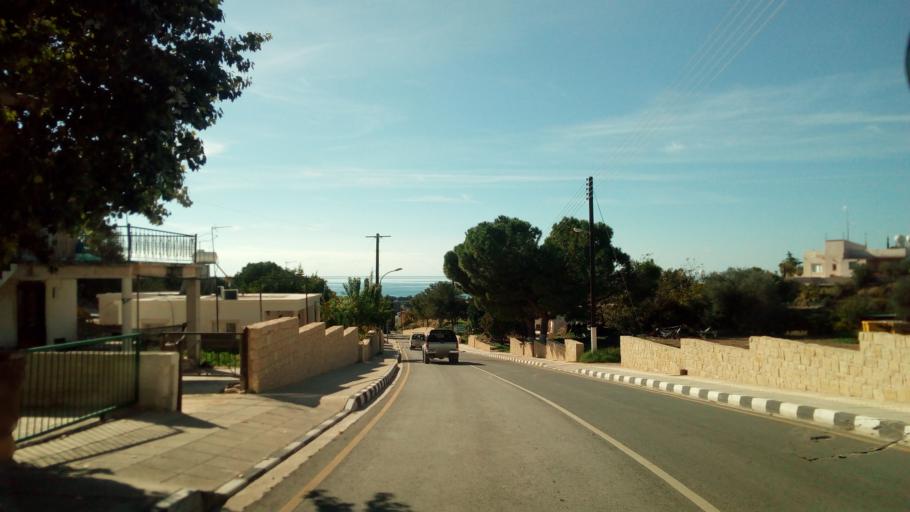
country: CY
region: Limassol
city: Pissouri
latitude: 34.7096
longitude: 32.5725
